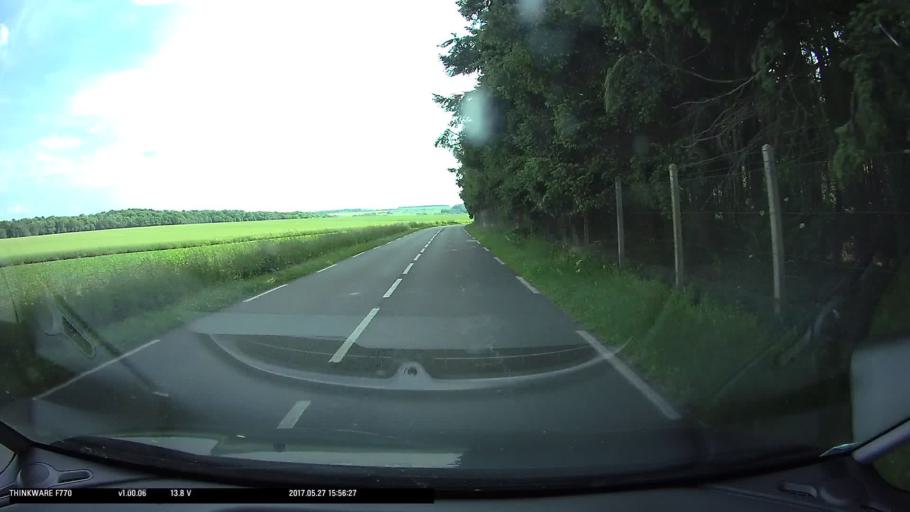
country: FR
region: Ile-de-France
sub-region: Departement du Val-d'Oise
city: Us
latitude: 49.1137
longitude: 1.9808
